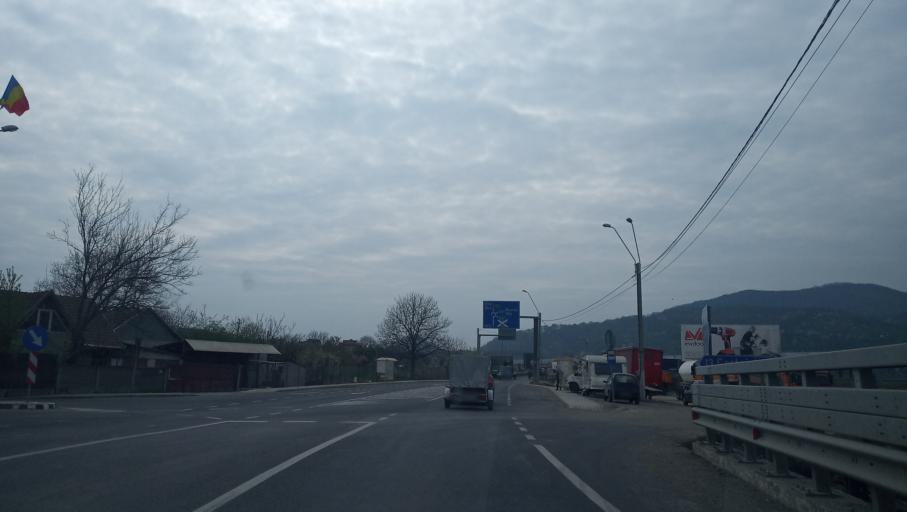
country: RO
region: Hunedoara
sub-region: Comuna Soimus
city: Soimus
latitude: 45.9161
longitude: 22.8770
